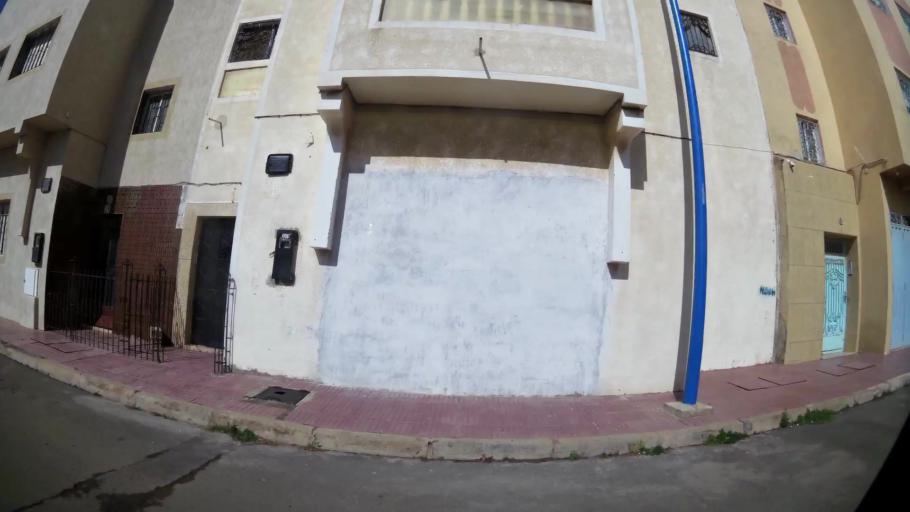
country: MA
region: Grand Casablanca
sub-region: Casablanca
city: Casablanca
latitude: 33.5645
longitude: -7.6967
